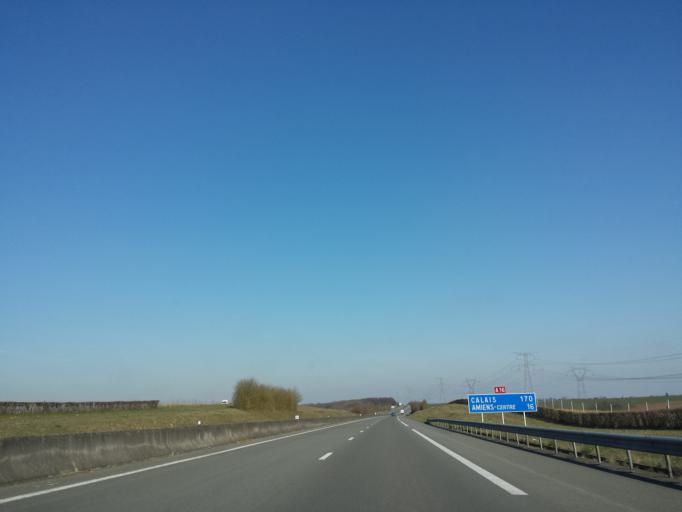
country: FR
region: Picardie
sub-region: Departement de la Somme
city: Conty
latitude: 49.7694
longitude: 2.2331
